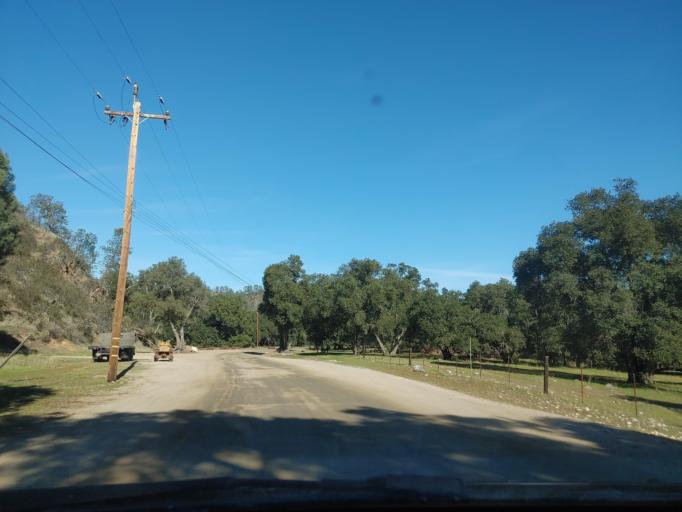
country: US
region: California
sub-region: San Benito County
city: Ridgemark
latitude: 36.6881
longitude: -121.3442
